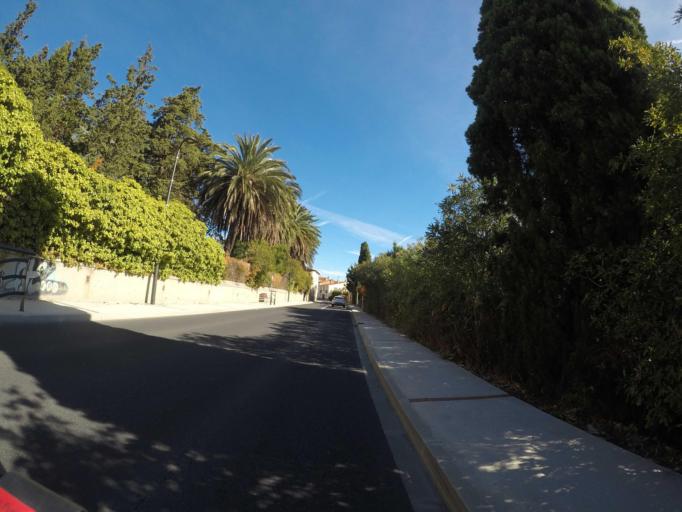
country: FR
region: Languedoc-Roussillon
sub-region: Departement des Pyrenees-Orientales
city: Ponteilla
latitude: 42.6246
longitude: 2.8131
